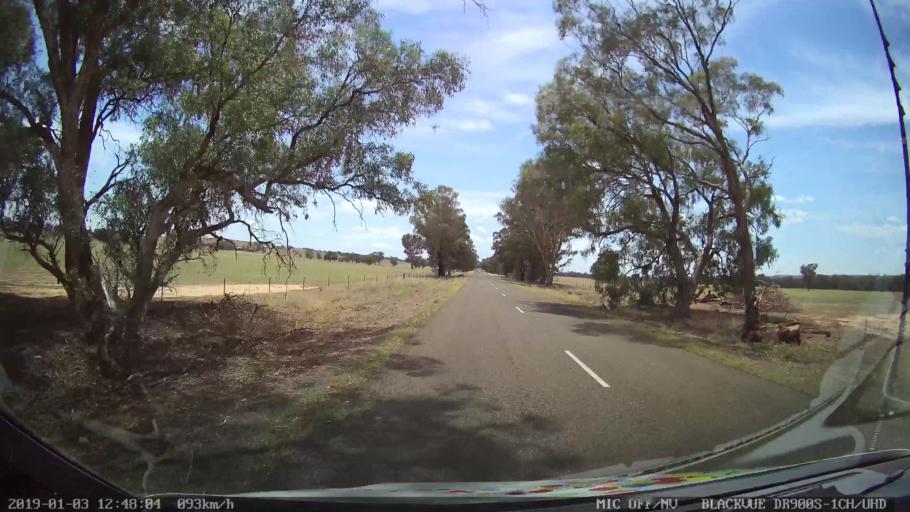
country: AU
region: New South Wales
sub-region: Weddin
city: Grenfell
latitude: -33.7190
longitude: 148.2473
